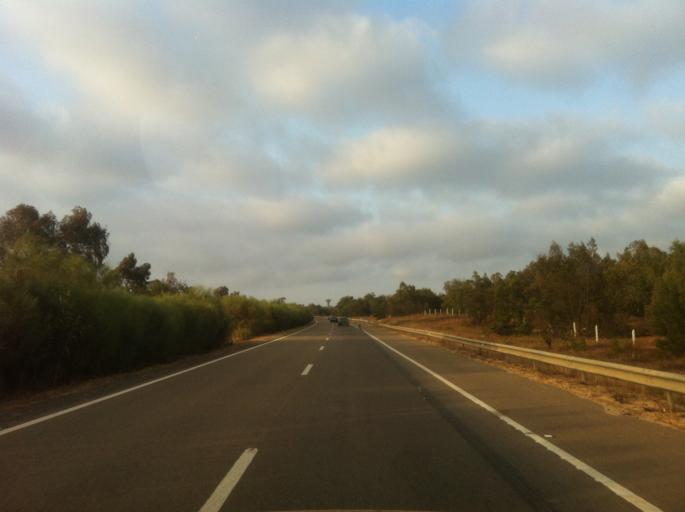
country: MA
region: Gharb-Chrarda-Beni Hssen
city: Sidi Yahia el Gharb
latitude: 34.6470
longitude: -6.4045
